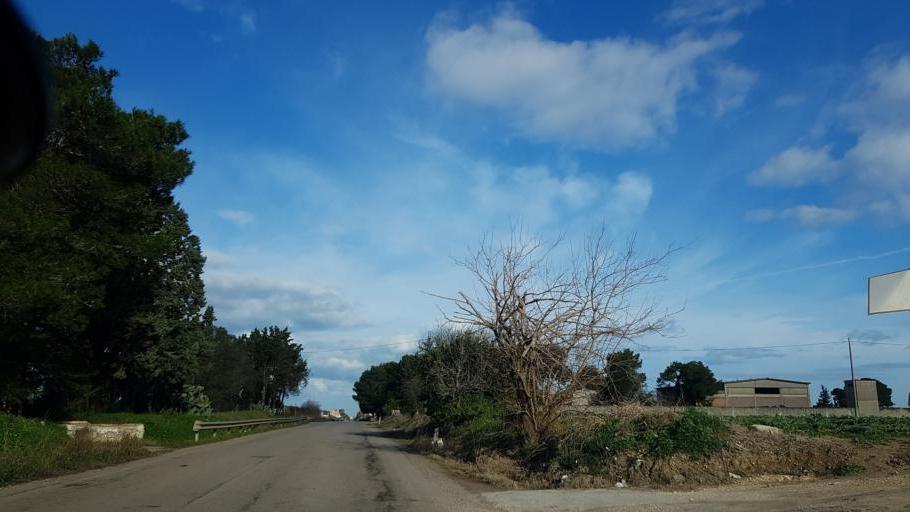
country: IT
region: Apulia
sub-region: Provincia di Brindisi
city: La Rosa
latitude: 40.5962
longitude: 17.9587
